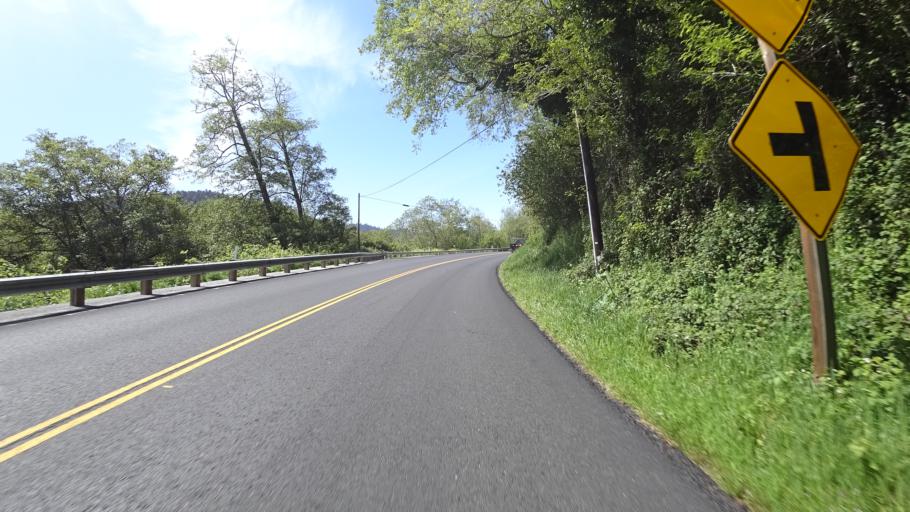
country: US
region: California
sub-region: Humboldt County
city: Westhaven-Moonstone
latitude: 41.3033
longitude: -124.0444
